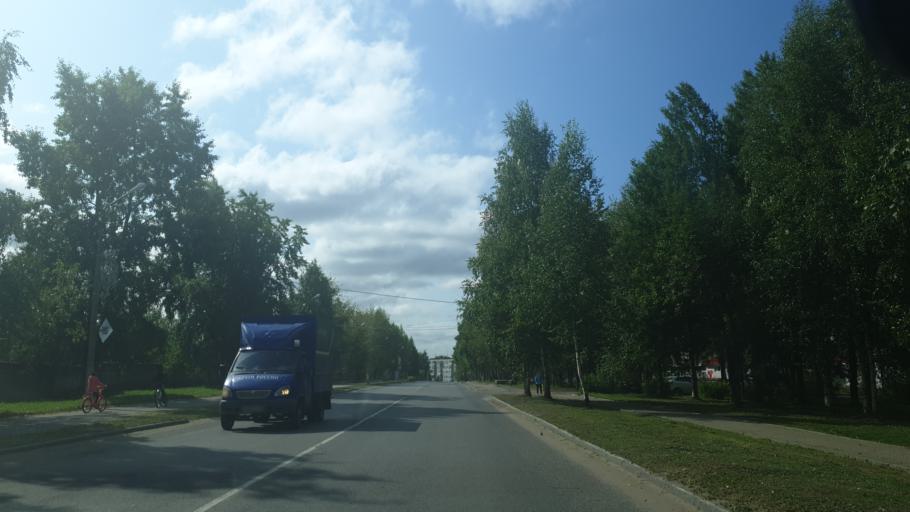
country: RU
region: Komi Republic
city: Ezhva
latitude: 61.7939
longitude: 50.7507
